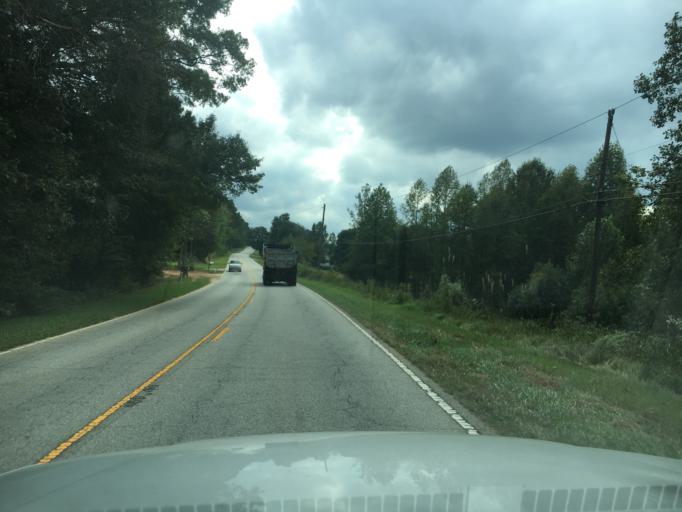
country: US
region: South Carolina
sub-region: Greenville County
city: Greer
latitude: 35.0177
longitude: -82.2644
